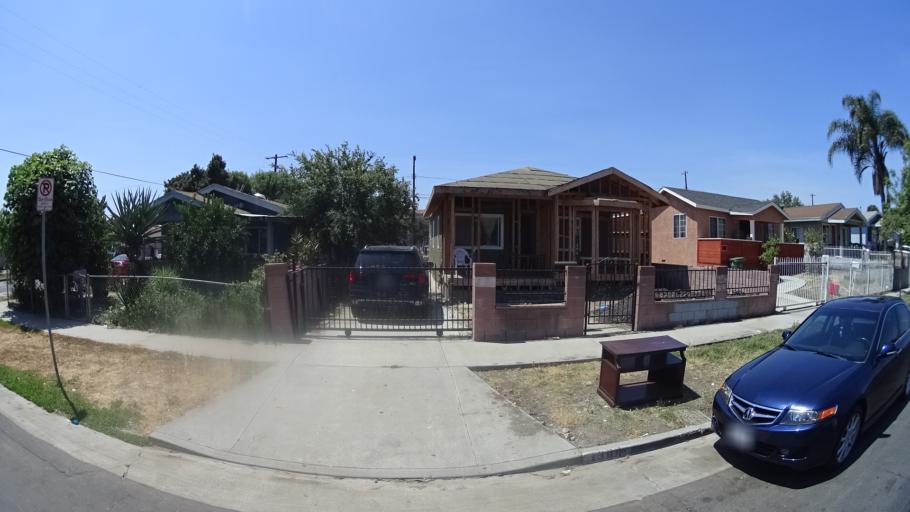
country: US
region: California
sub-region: Los Angeles County
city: Westmont
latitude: 33.9728
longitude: -118.2983
